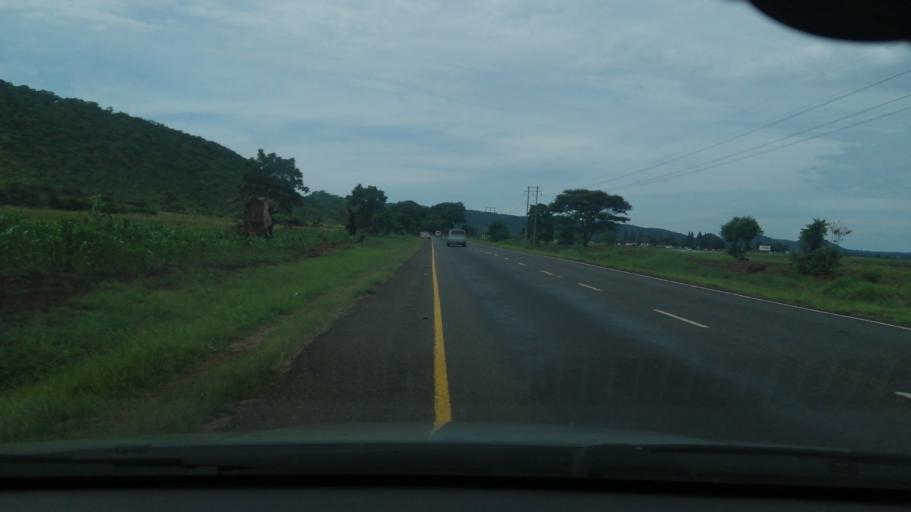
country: ZW
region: Mashonaland West
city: Norton
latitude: -17.8465
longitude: 30.7986
